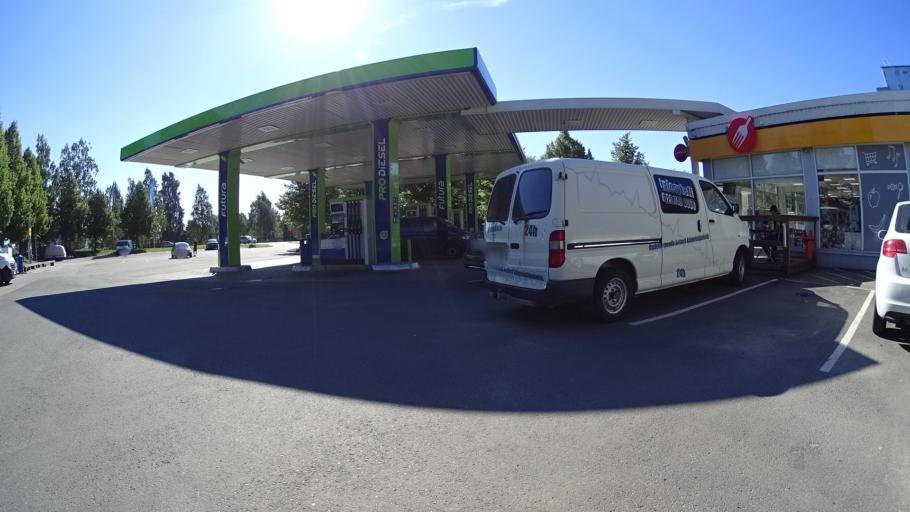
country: FI
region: Uusimaa
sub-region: Helsinki
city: Teekkarikylae
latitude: 60.2761
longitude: 24.8551
